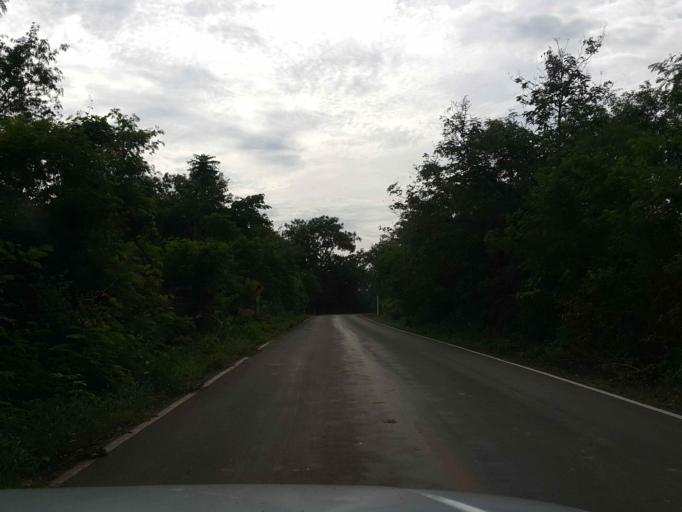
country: TH
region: Sukhothai
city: Thung Saliam
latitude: 17.3126
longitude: 99.5220
